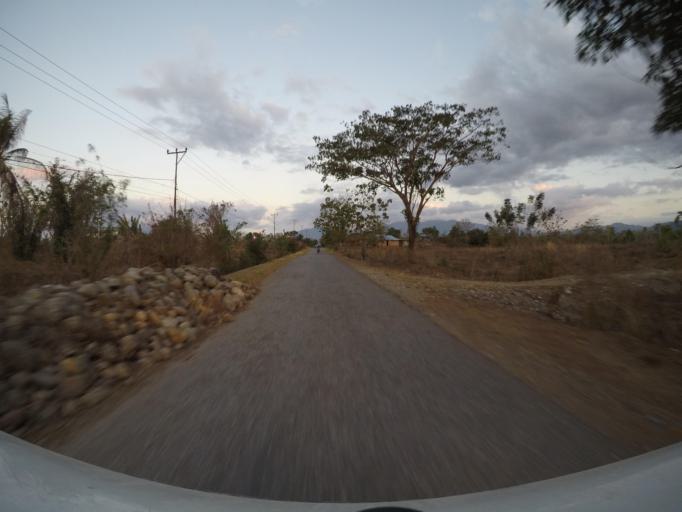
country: TL
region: Bobonaro
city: Maliana
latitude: -8.9724
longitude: 125.1350
